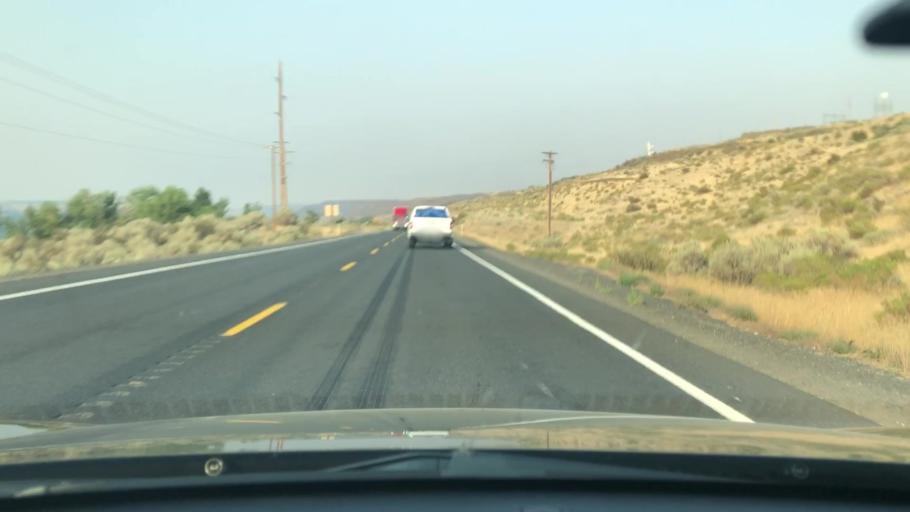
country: US
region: Oregon
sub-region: Umatilla County
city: Stanfield
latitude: 45.9207
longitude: -119.1218
